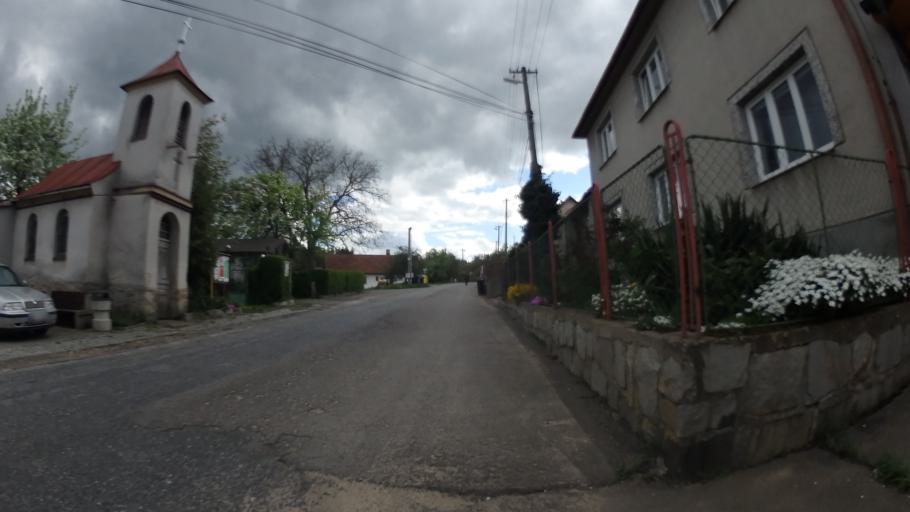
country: CZ
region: Vysocina
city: Merin
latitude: 49.3663
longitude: 15.8825
